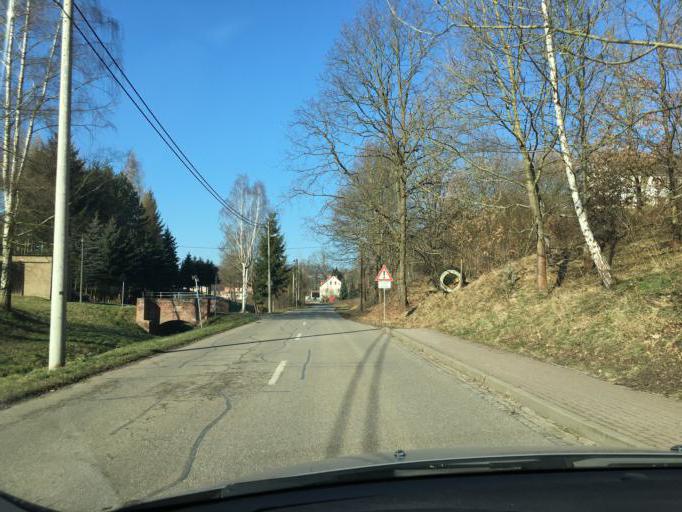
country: DE
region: Saxony
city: Lunzenau
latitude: 50.9629
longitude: 12.7382
